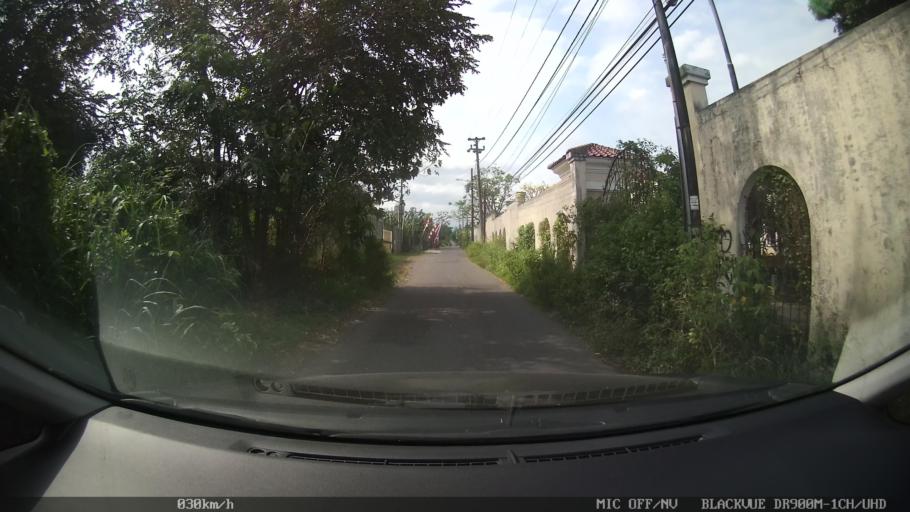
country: ID
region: Daerah Istimewa Yogyakarta
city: Depok
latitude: -7.7607
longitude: 110.4187
